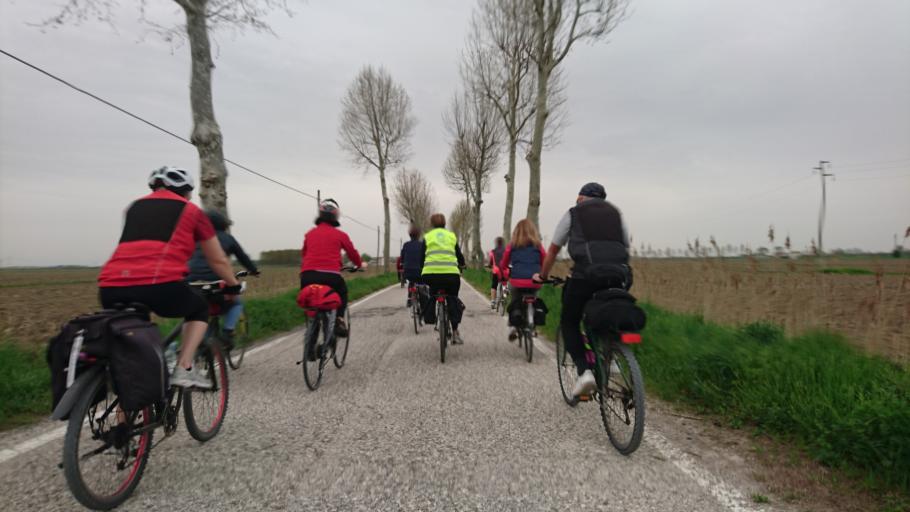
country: IT
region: Veneto
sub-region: Provincia di Venezia
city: Lugugnana
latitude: 45.6881
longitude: 12.9734
